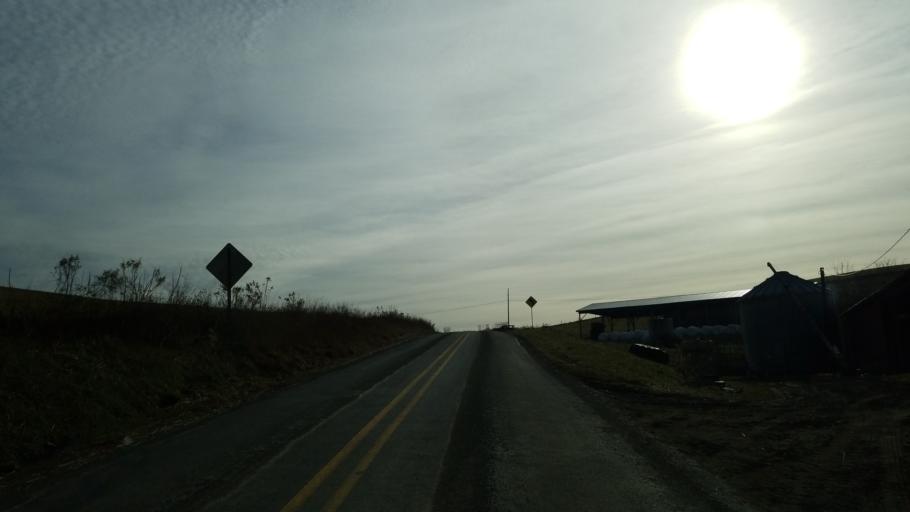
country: US
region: Pennsylvania
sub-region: Jefferson County
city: Albion
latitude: 40.9522
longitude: -78.9224
